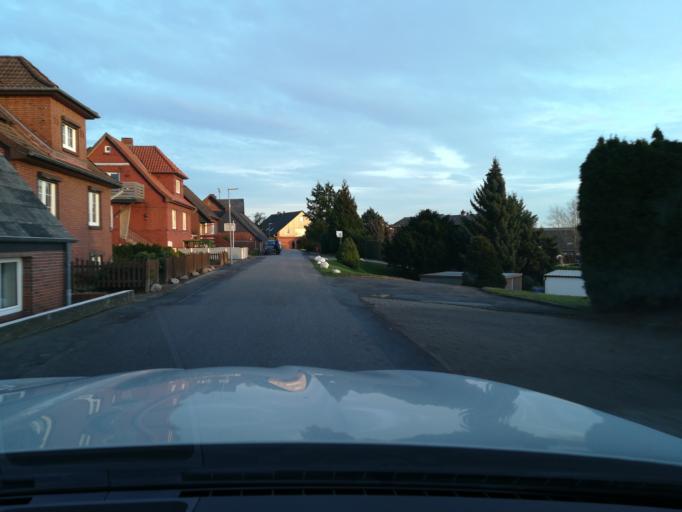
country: DE
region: Lower Saxony
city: Stelle
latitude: 53.4405
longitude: 10.0863
